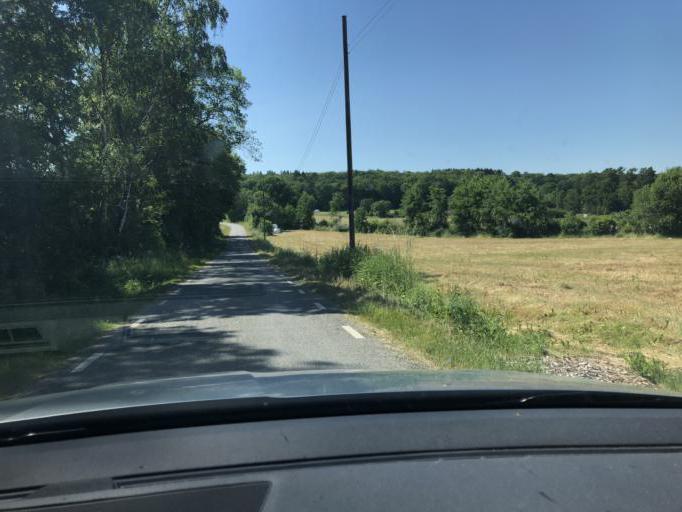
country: SE
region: Blekinge
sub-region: Solvesborgs Kommun
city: Soelvesborg
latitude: 56.1354
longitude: 14.6136
